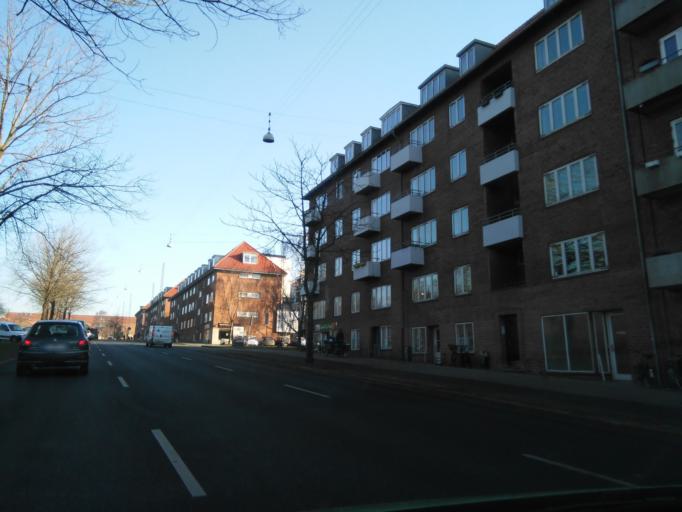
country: DK
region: Central Jutland
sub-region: Arhus Kommune
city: Arhus
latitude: 56.1586
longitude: 10.1830
